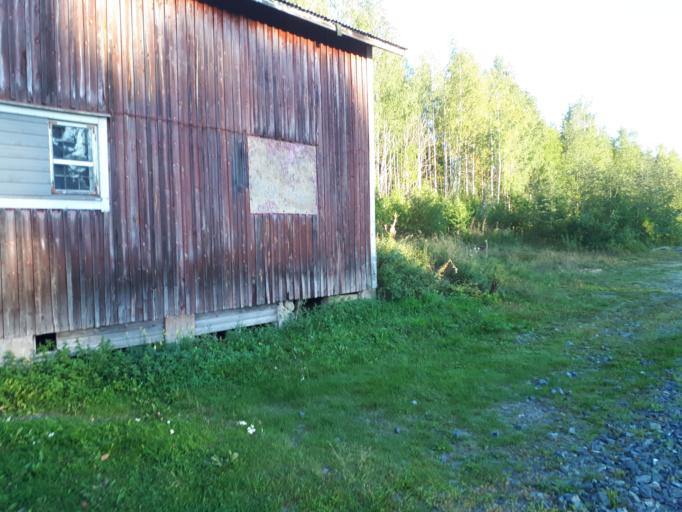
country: FI
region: Northern Ostrobothnia
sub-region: Oulunkaari
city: Ii
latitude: 65.3192
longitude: 25.4426
